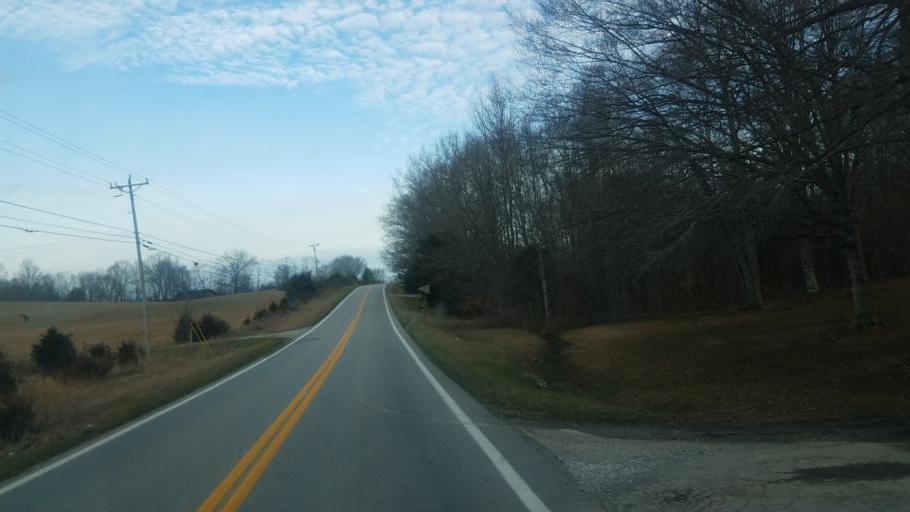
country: US
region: Kentucky
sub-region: Clinton County
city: Albany
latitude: 36.7781
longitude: -85.1742
